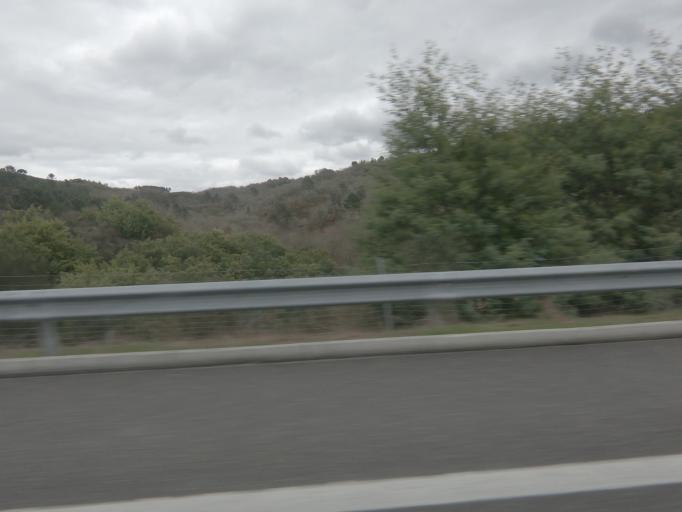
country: ES
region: Galicia
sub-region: Provincia de Ourense
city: Punxin
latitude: 42.3612
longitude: -7.9964
